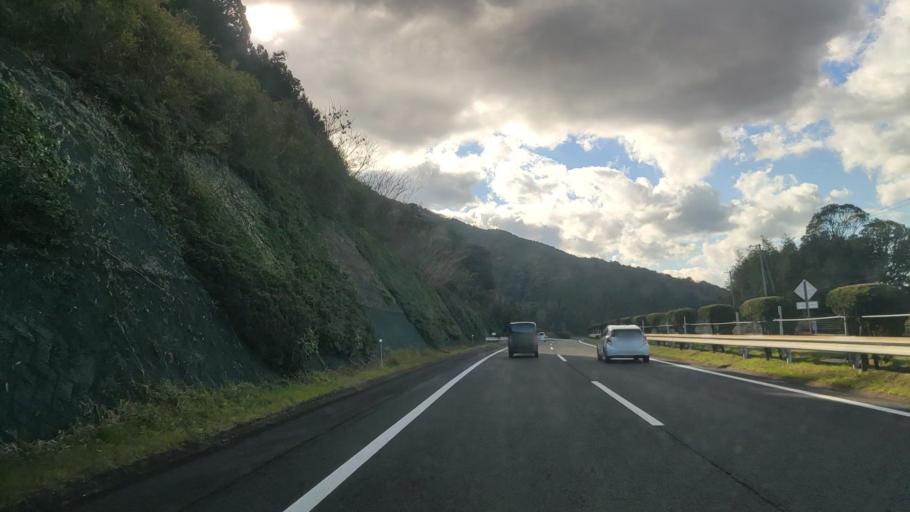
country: JP
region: Ehime
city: Niihama
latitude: 33.9373
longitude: 133.3801
